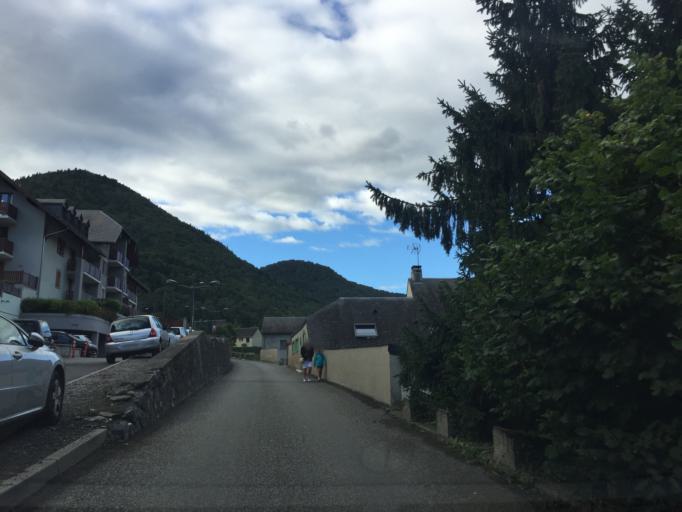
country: FR
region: Midi-Pyrenees
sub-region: Departement des Hautes-Pyrenees
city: Saint-Lary-Soulan
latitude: 42.9024
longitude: 0.3586
